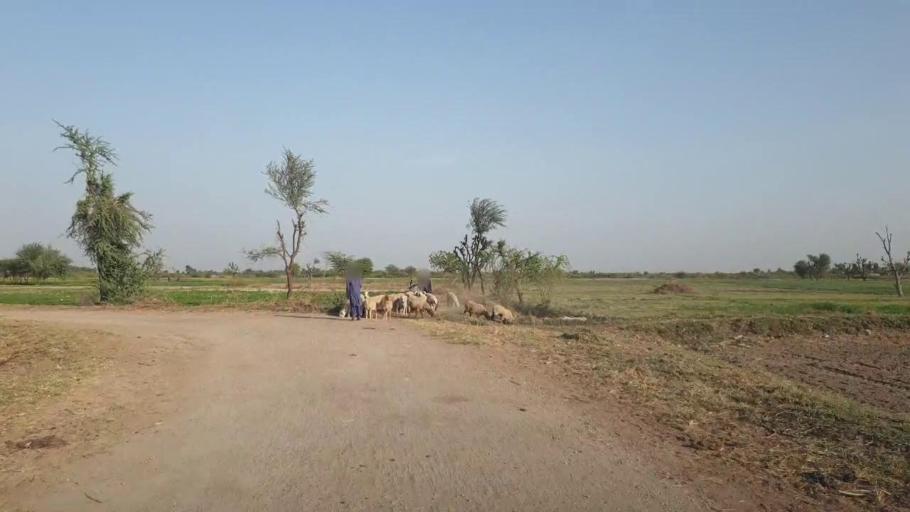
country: PK
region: Sindh
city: Dhoro Naro
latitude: 25.4947
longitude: 69.5824
